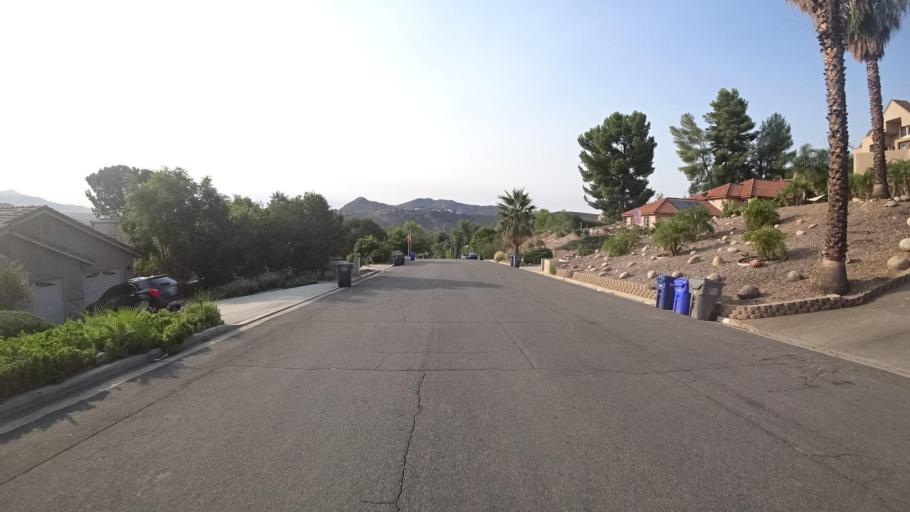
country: US
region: California
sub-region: San Diego County
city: San Diego Country Estates
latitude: 33.0119
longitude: -116.8262
